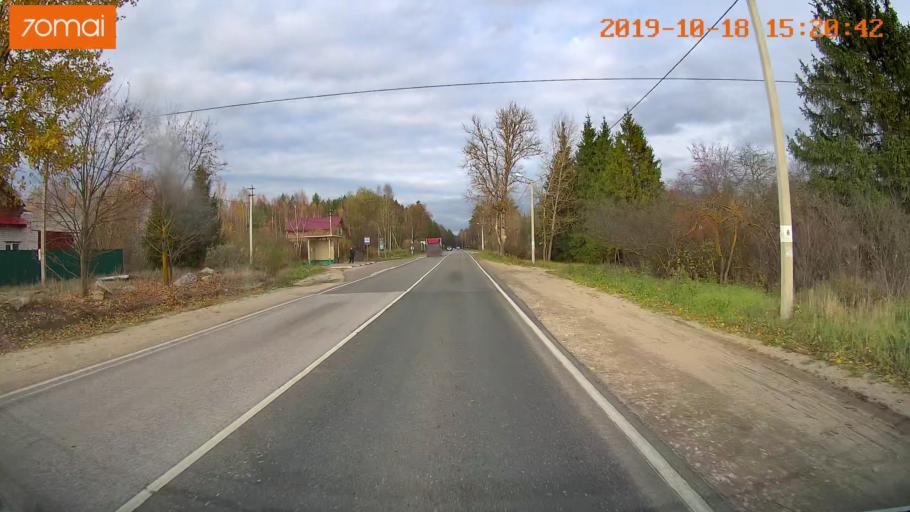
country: RU
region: Vladimir
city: Anopino
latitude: 55.6894
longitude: 40.7462
